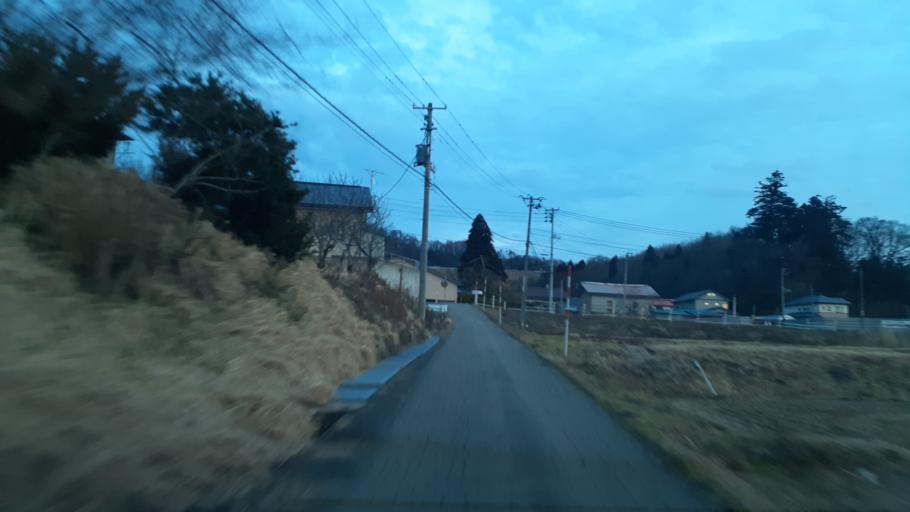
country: JP
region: Fukushima
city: Kitakata
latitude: 37.5245
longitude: 139.9547
